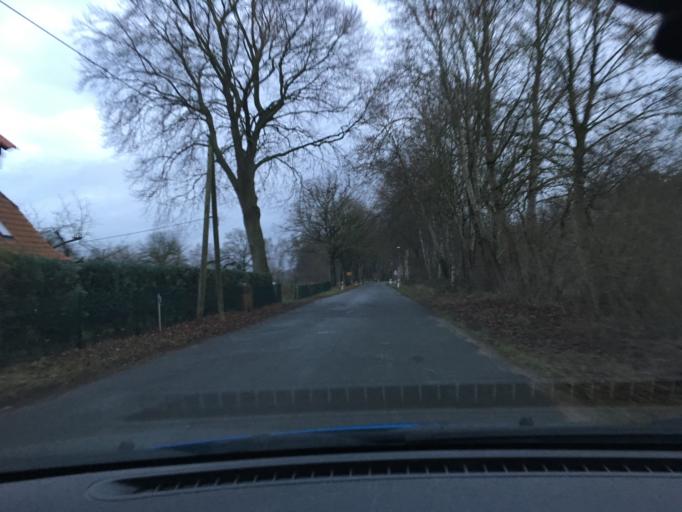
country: DE
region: Mecklenburg-Vorpommern
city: Boizenburg
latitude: 53.3870
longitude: 10.6906
